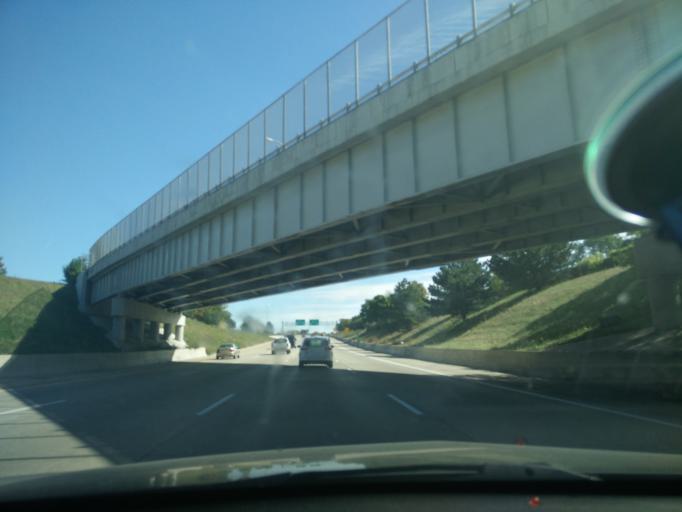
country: US
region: Michigan
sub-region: Macomb County
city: Roseville
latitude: 42.4947
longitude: -82.9243
